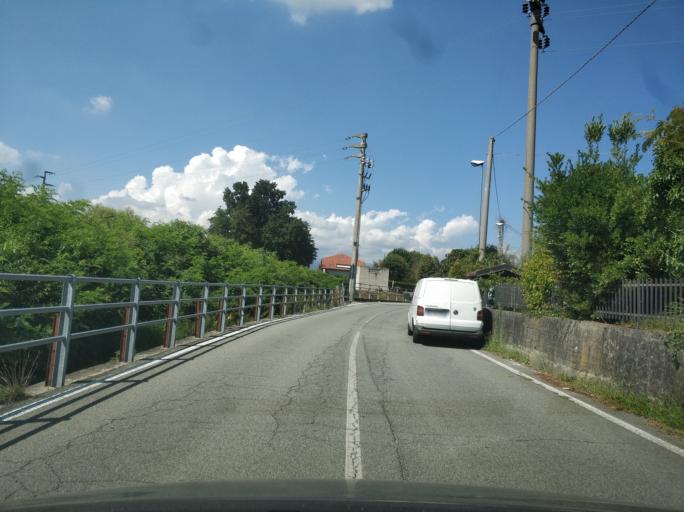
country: IT
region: Piedmont
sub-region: Provincia di Torino
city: Rivarolo Canavese
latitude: 45.3228
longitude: 7.7200
